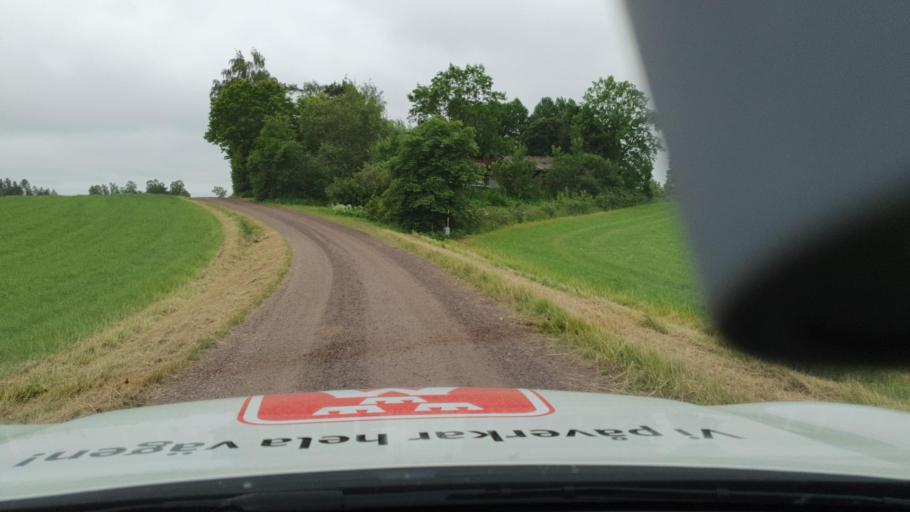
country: SE
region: Vaestra Goetaland
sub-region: Tidaholms Kommun
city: Olofstorp
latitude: 58.3893
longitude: 13.9996
